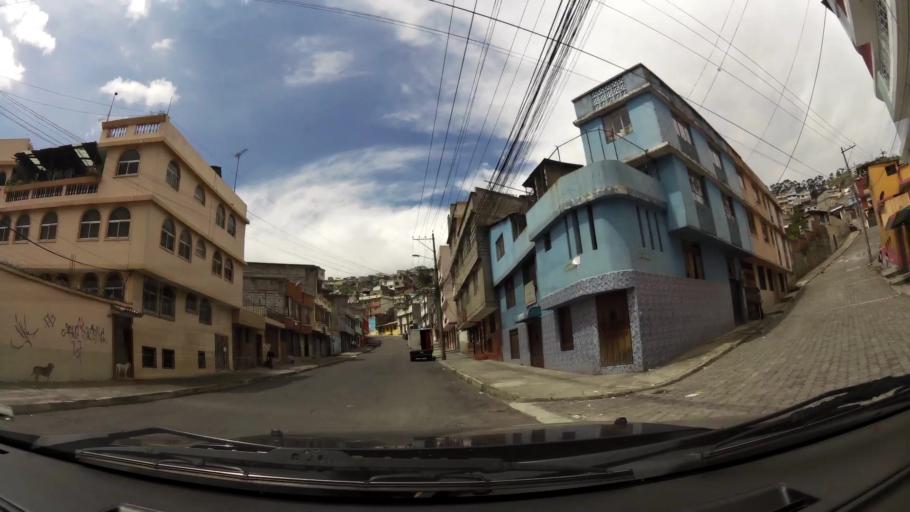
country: EC
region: Pichincha
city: Quito
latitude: -0.2550
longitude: -78.5123
